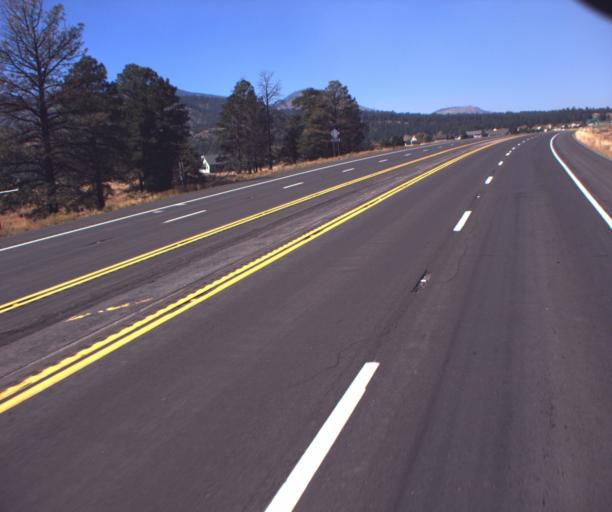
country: US
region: Arizona
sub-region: Coconino County
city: Flagstaff
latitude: 35.3409
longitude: -111.5579
